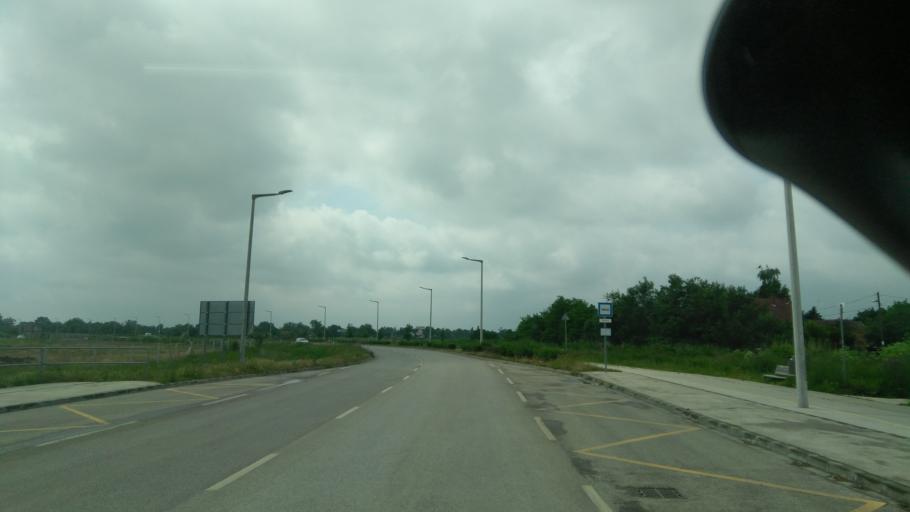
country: HU
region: Bekes
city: Bekescsaba
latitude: 46.6561
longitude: 21.0869
